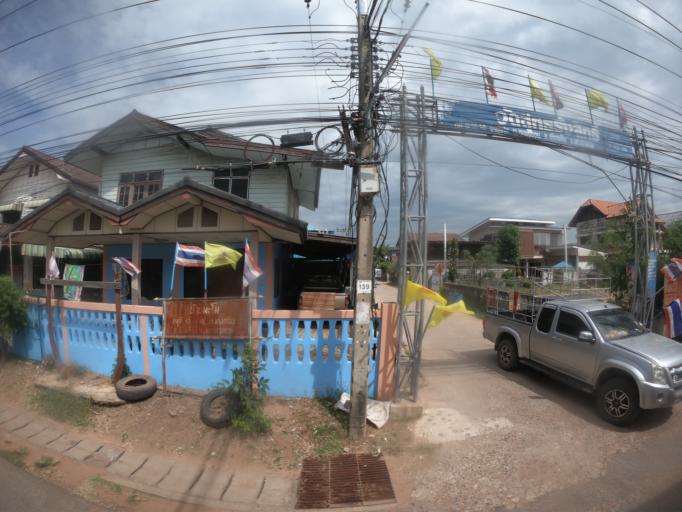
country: TH
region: Maha Sarakham
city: Chiang Yuen
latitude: 16.3440
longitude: 103.1487
